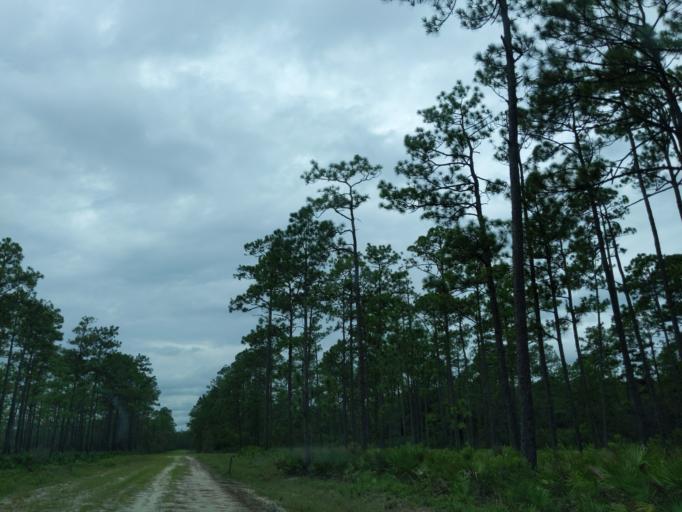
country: US
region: Florida
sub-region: Gadsden County
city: Midway
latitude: 30.3604
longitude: -84.4919
